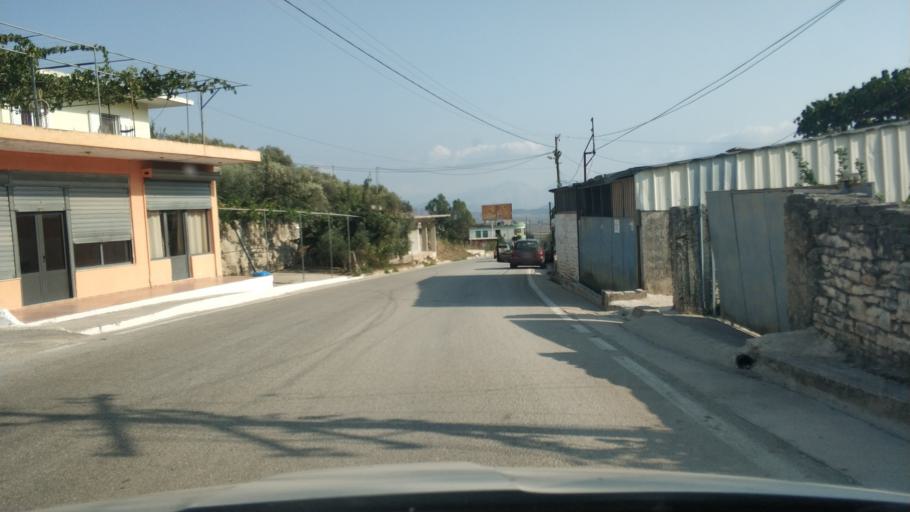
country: AL
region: Vlore
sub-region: Rrethi i Sarandes
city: Sarande
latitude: 39.8768
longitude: 20.0259
